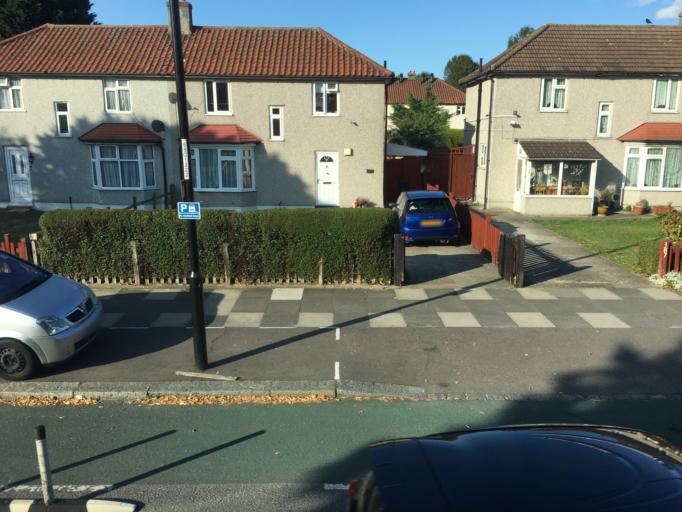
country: GB
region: England
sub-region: Greater London
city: Blackheath
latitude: 51.4610
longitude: 0.0425
